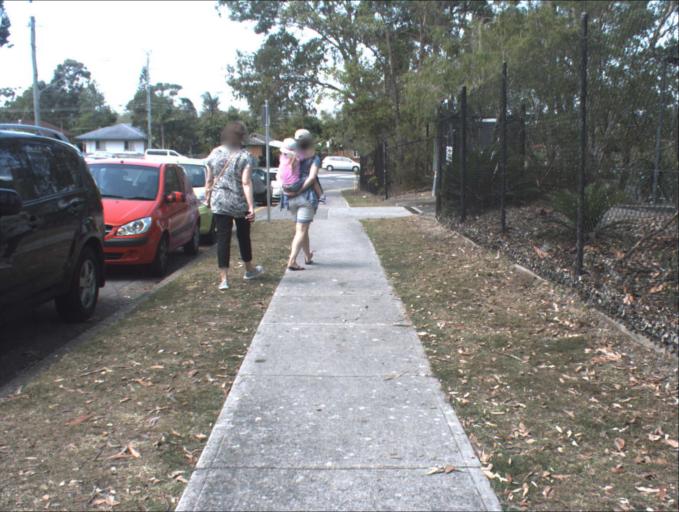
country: AU
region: Queensland
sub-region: Logan
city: Logan City
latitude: -27.6463
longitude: 153.1057
